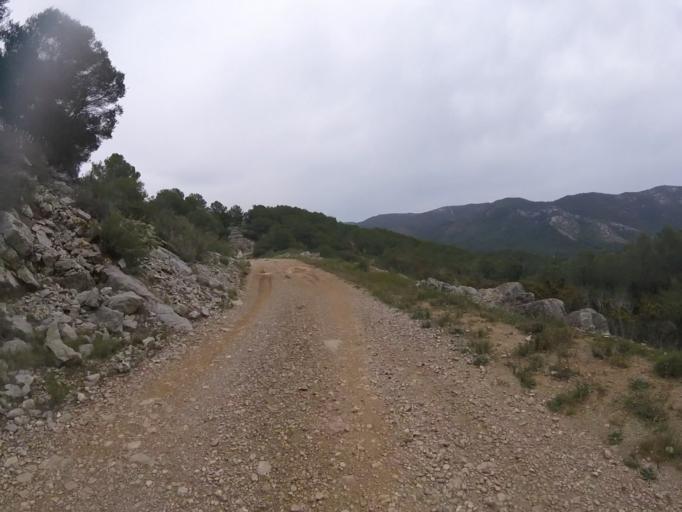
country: ES
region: Valencia
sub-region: Provincia de Castello
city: Alcala de Xivert
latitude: 40.3117
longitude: 0.2637
